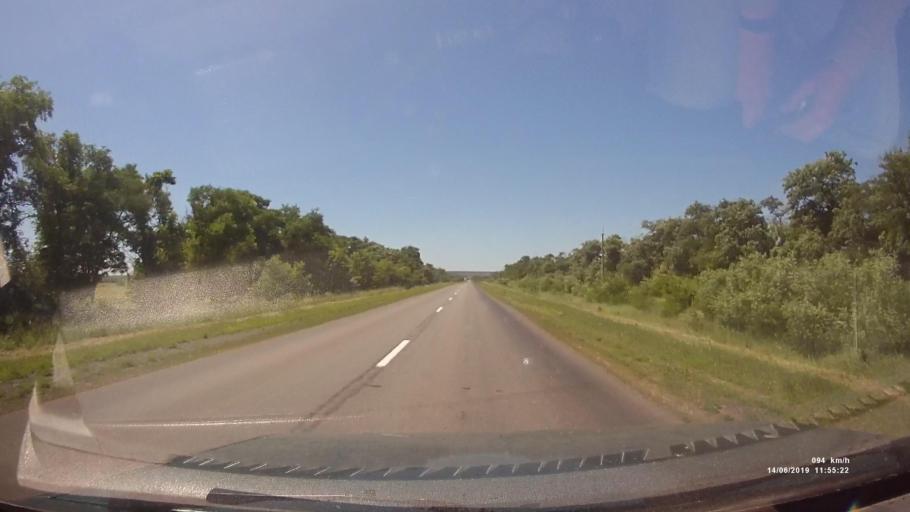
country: RU
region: Rostov
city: Kazanskaya
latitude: 49.8111
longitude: 41.1783
